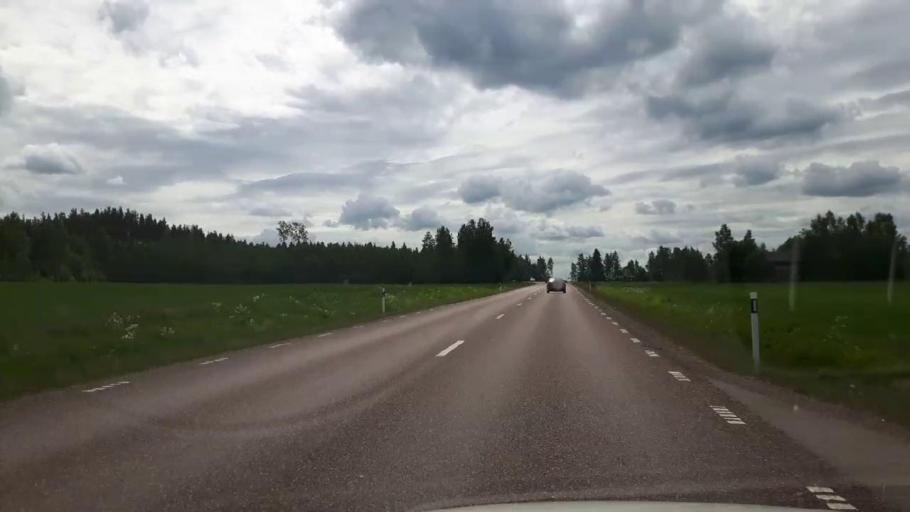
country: SE
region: Dalarna
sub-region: Hedemora Kommun
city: Hedemora
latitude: 60.3400
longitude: 15.9454
